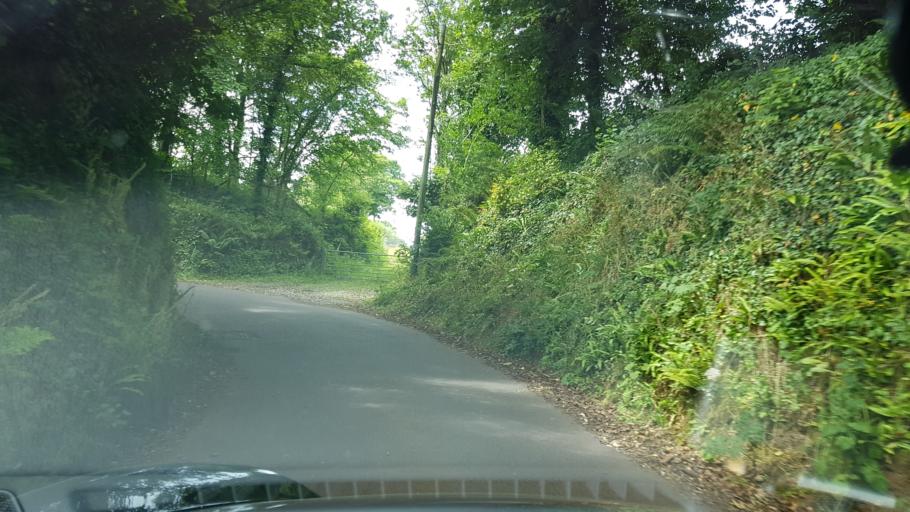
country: GB
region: Wales
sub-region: Carmarthenshire
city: Saint Clears
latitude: 51.7698
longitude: -4.4712
